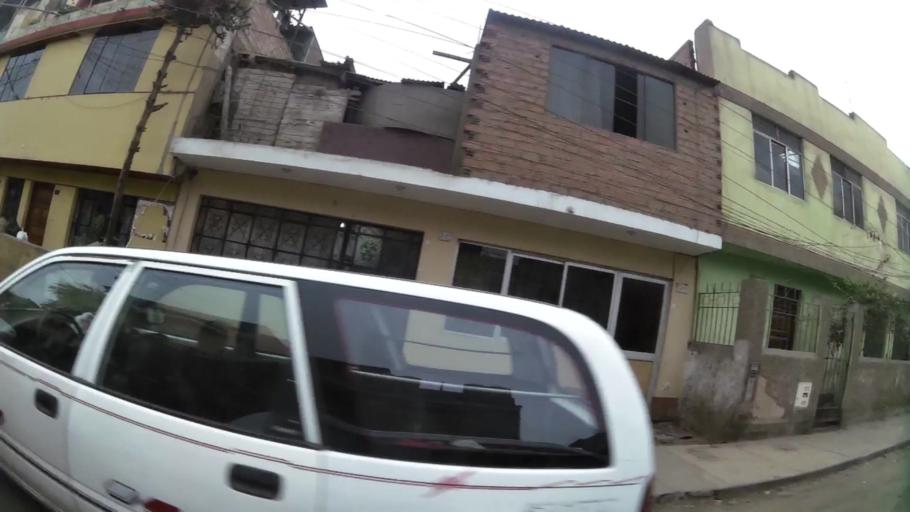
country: PE
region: Lima
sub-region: Lima
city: Surco
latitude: -12.1487
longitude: -76.9789
